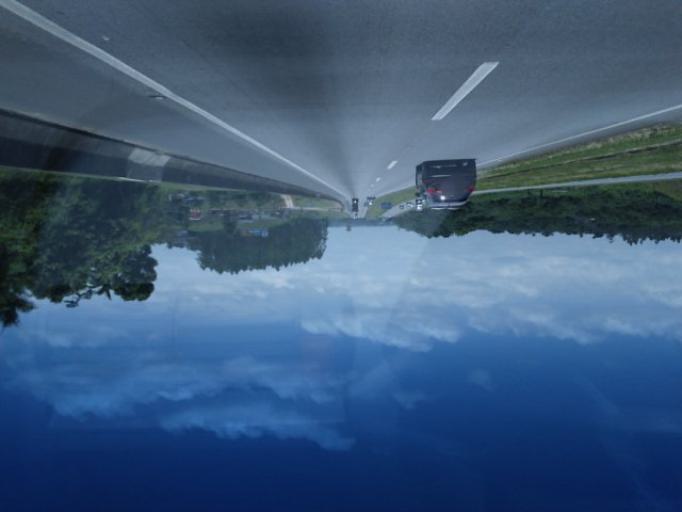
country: BR
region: Sao Paulo
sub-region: Registro
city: Registro
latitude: -24.4691
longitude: -47.8227
